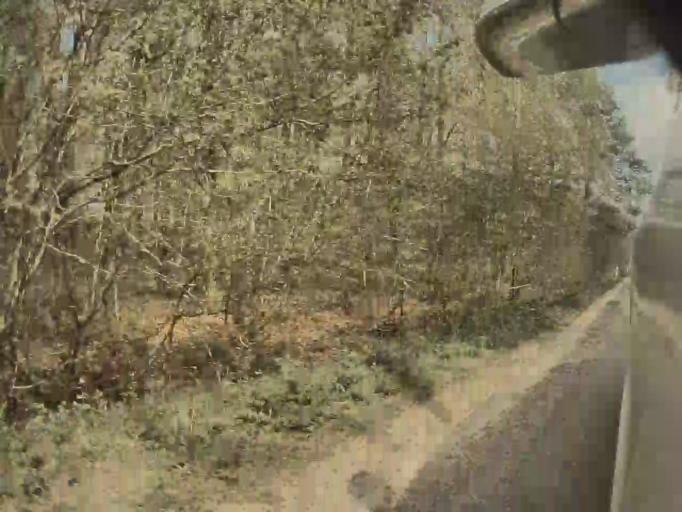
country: BE
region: Wallonia
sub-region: Province du Luxembourg
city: Tellin
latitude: 50.0581
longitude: 5.2083
